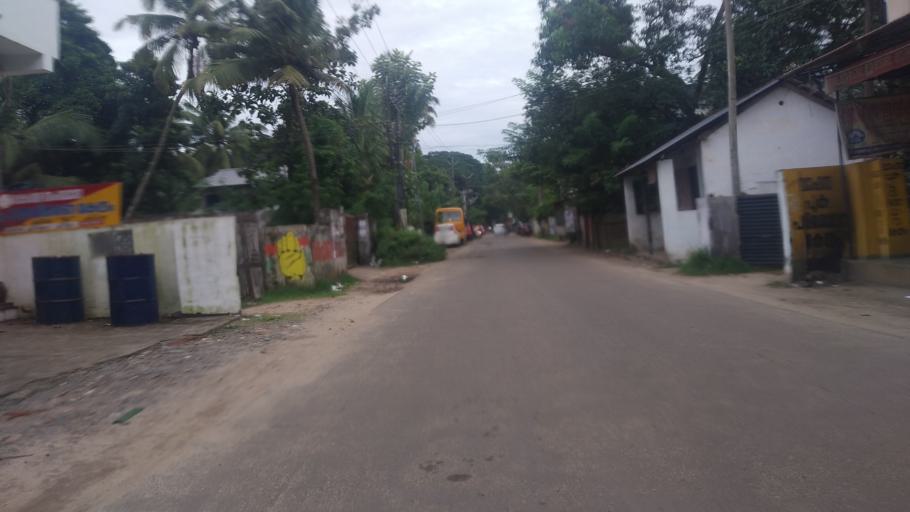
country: IN
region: Kerala
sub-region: Alappuzha
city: Arukutti
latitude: 9.8707
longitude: 76.2906
